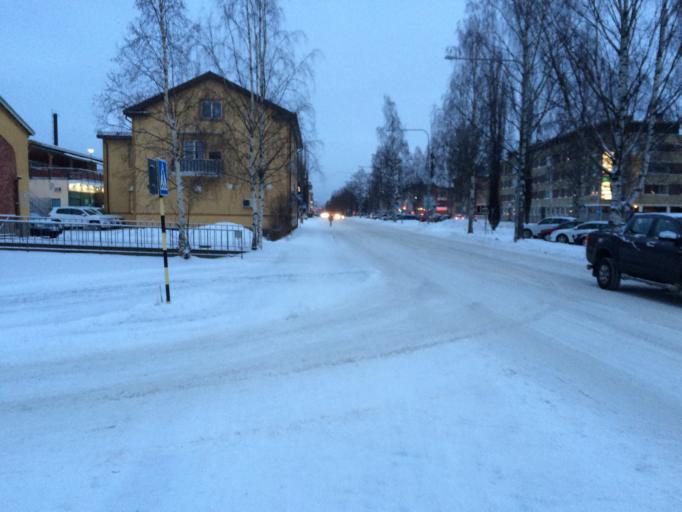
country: SE
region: Vaesterbotten
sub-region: Skelleftea Kommun
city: Skelleftea
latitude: 64.7523
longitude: 20.9474
